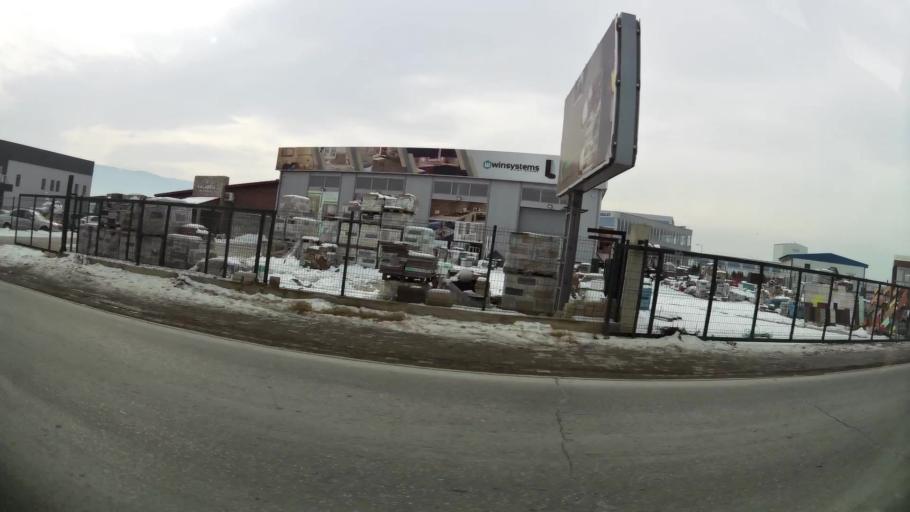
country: MK
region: Suto Orizari
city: Suto Orizare
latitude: 42.0360
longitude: 21.3991
